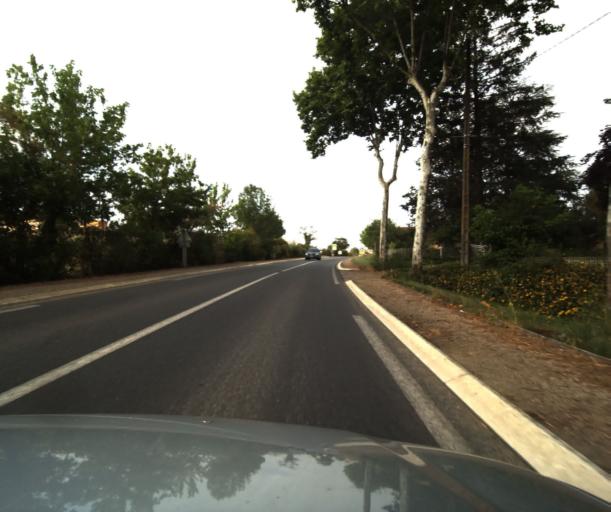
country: FR
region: Midi-Pyrenees
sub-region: Departement du Tarn-et-Garonne
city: Beaumont-de-Lomagne
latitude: 43.8878
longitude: 1.0006
